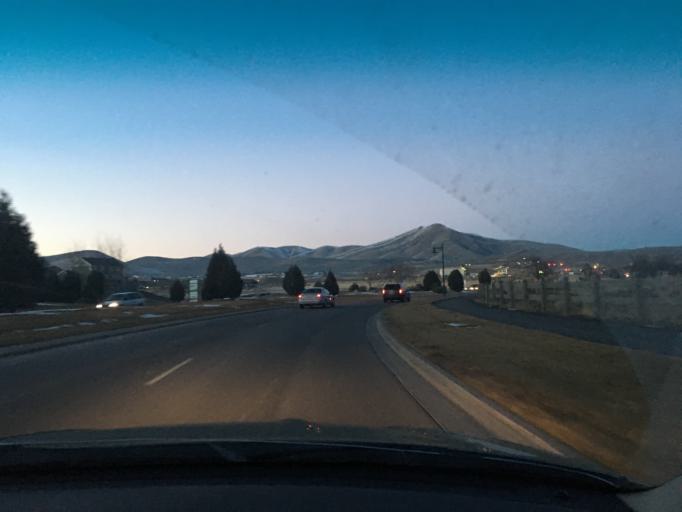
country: US
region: Utah
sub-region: Utah County
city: Eagle Mountain
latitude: 40.3762
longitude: -111.9747
